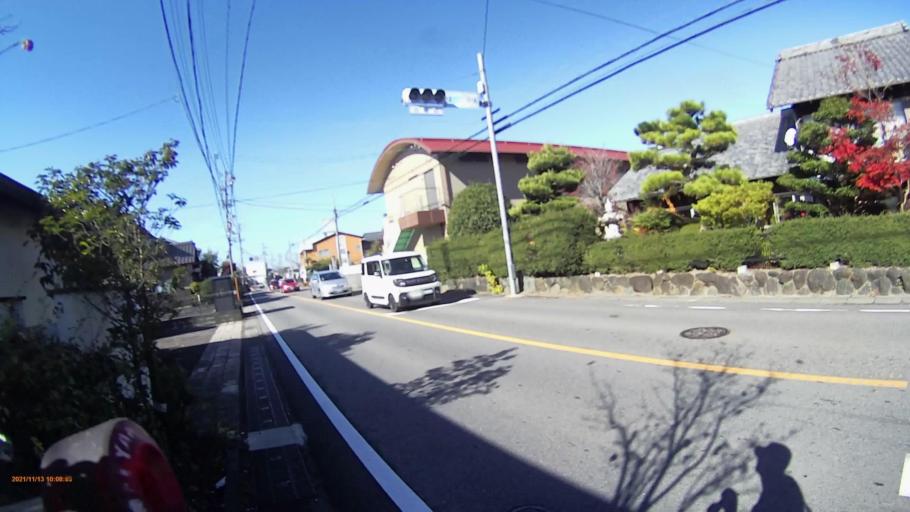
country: JP
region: Gifu
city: Minokamo
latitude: 35.4347
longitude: 137.0360
